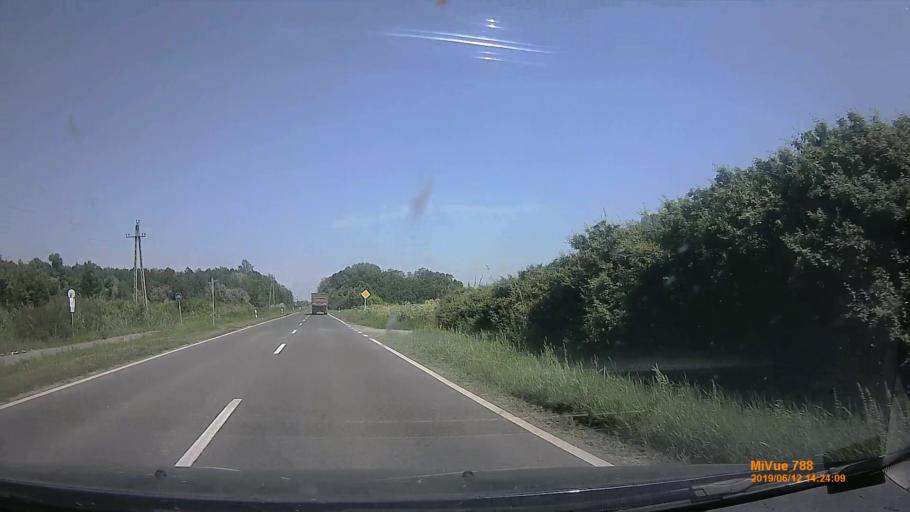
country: HU
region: Csongrad
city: Deszk
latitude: 46.2185
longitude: 20.3055
